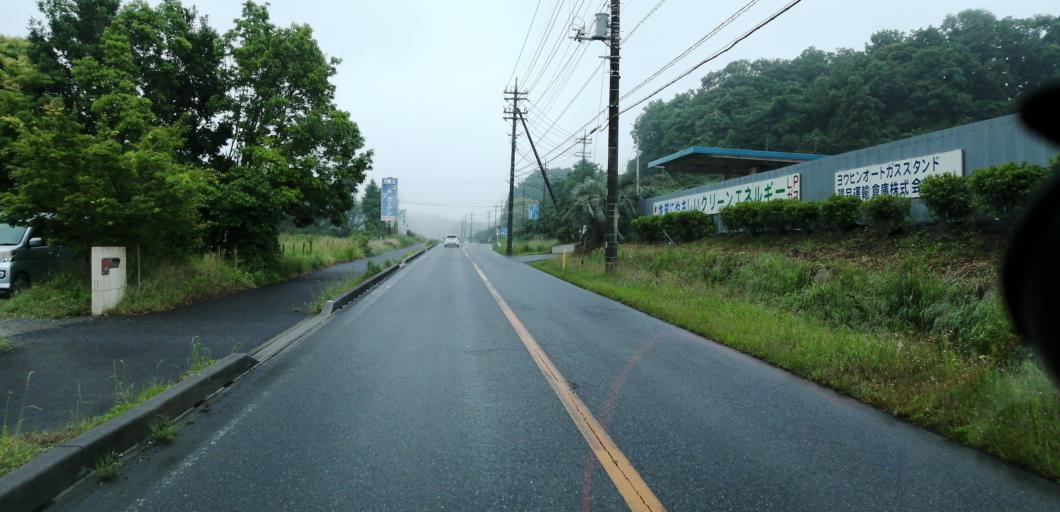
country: JP
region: Chiba
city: Ichihara
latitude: 35.4632
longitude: 140.1086
